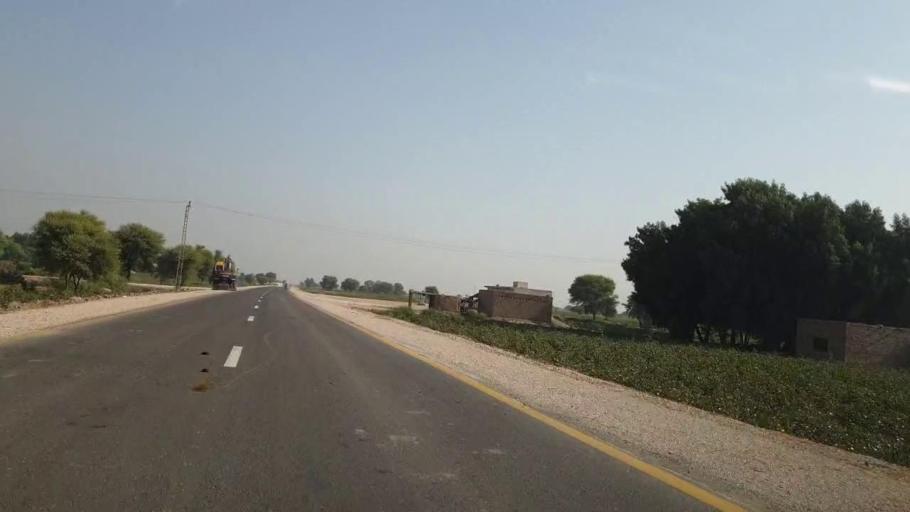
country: PK
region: Sindh
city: Sehwan
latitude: 26.4755
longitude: 67.7872
